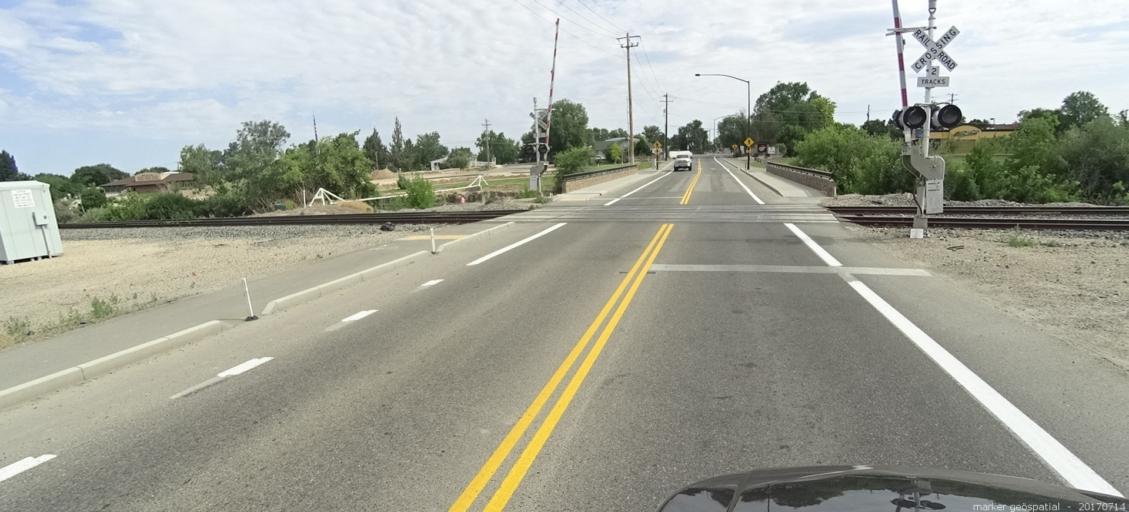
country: US
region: Idaho
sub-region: Ada County
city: Kuna
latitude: 43.4891
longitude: -116.4210
